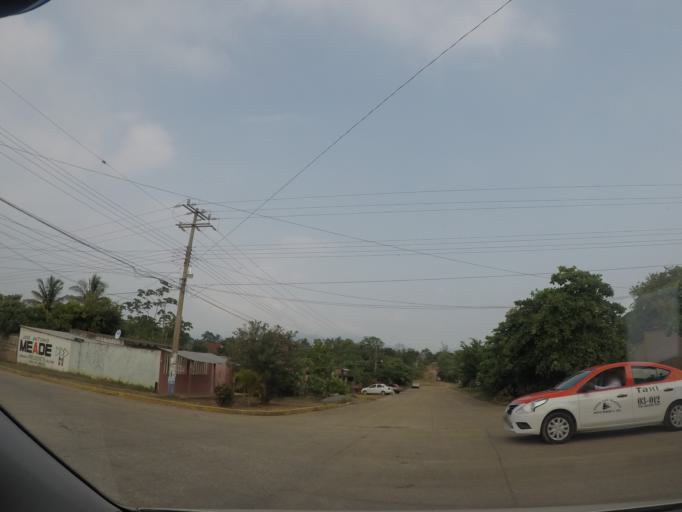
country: MX
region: Oaxaca
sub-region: Santa Maria Petapa
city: Llano Suchiapa
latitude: 16.8679
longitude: -95.0486
